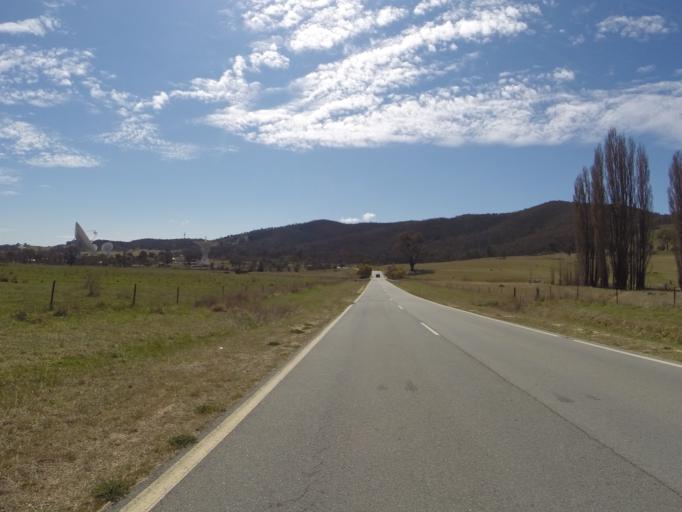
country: AU
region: Australian Capital Territory
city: Macarthur
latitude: -35.4095
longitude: 148.9817
